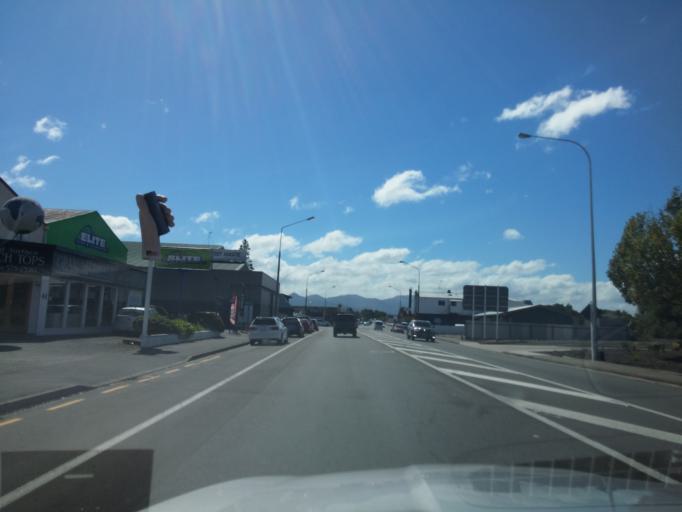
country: NZ
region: Marlborough
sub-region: Marlborough District
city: Blenheim
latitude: -41.5072
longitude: 173.9595
